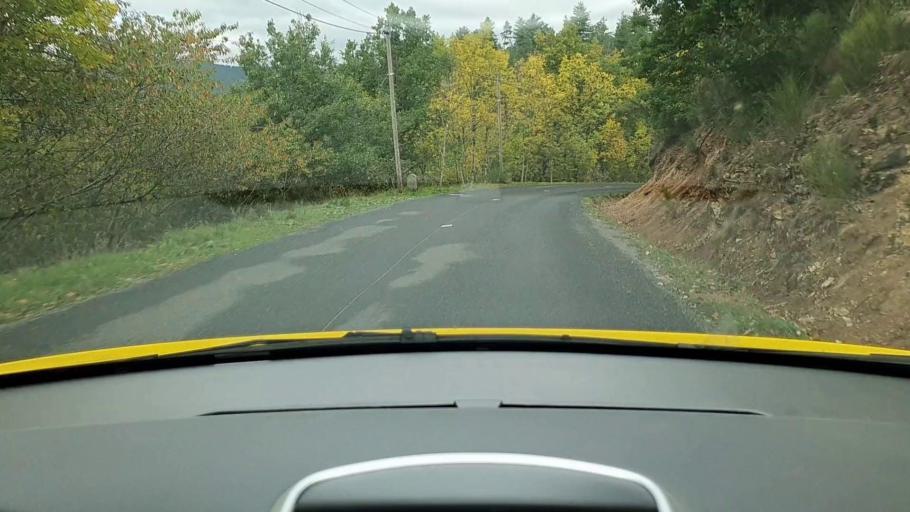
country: FR
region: Languedoc-Roussillon
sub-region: Departement de la Lozere
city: Meyrueis
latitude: 44.1071
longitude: 3.4379
